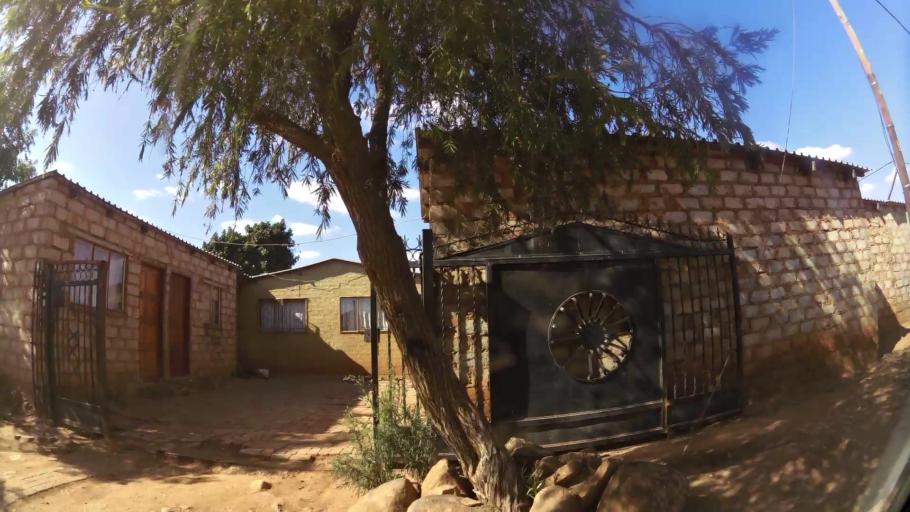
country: ZA
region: Gauteng
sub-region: City of Tshwane Metropolitan Municipality
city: Cullinan
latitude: -25.7205
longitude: 28.4062
